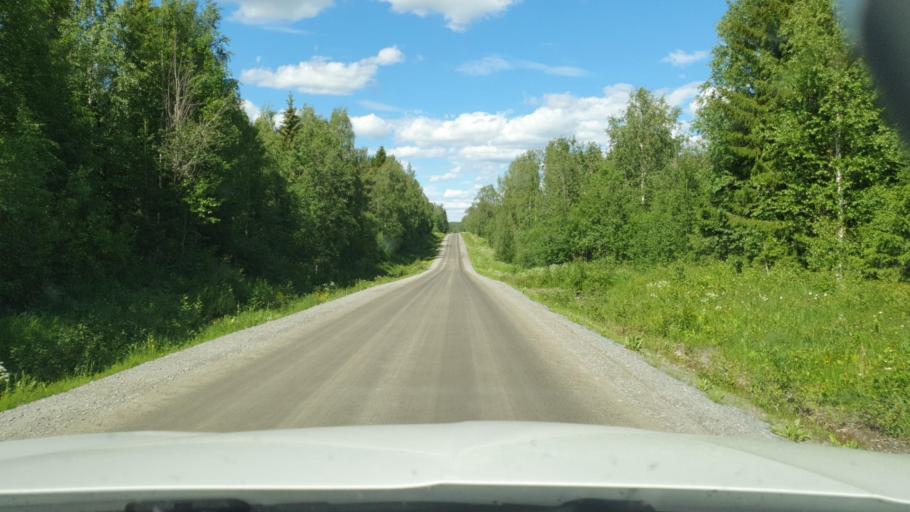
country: SE
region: Vaesterbotten
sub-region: Skelleftea Kommun
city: Forsbacka
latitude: 64.7790
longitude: 20.5151
